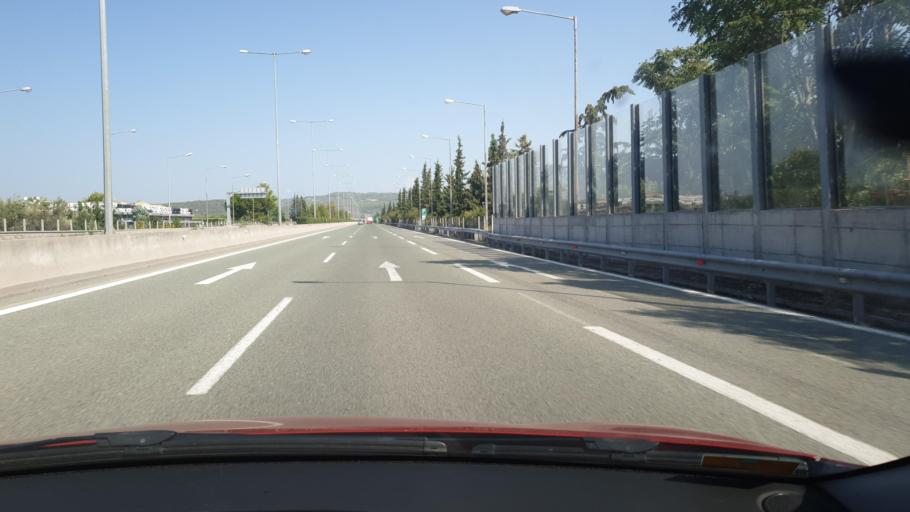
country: GR
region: Central Greece
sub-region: Nomos Fthiotidos
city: Martinon
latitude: 38.6217
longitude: 23.1263
